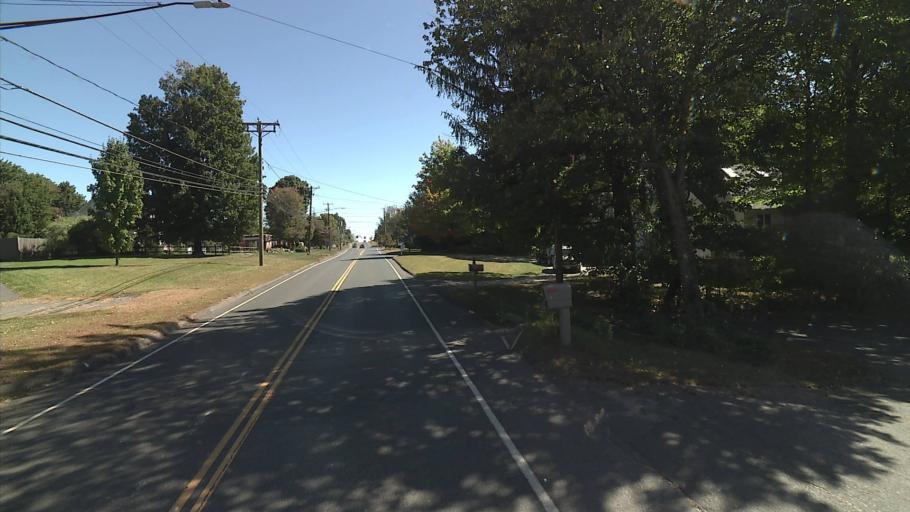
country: US
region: Connecticut
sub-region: New Haven County
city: Prospect
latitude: 41.5035
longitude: -72.9819
